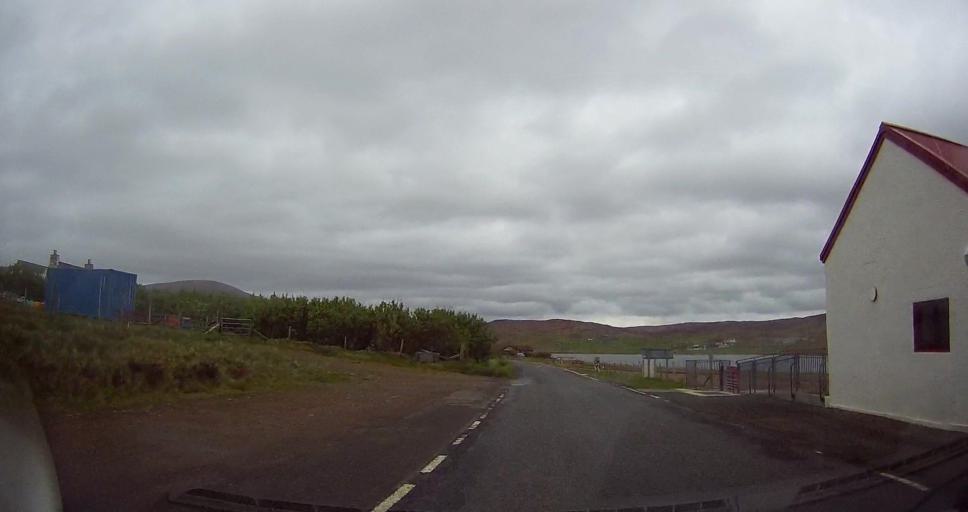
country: GB
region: Scotland
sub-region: Shetland Islands
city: Lerwick
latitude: 60.4838
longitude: -1.4721
